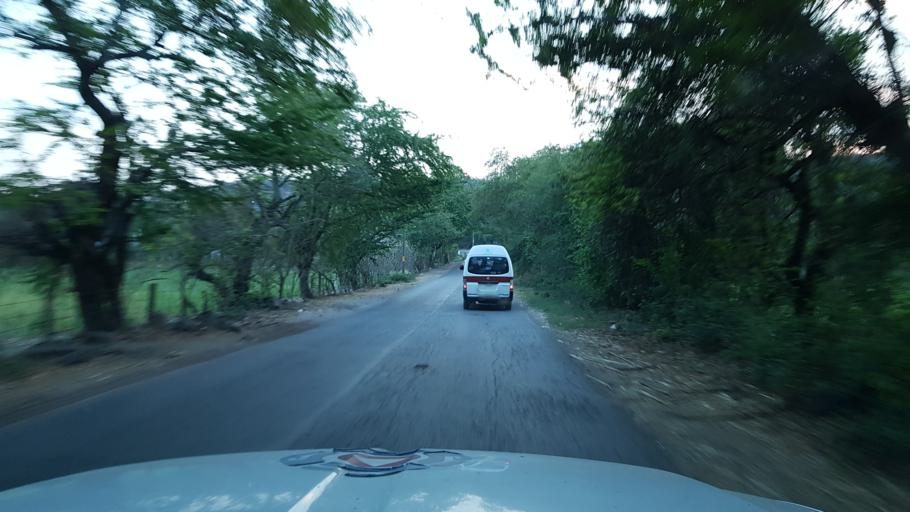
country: MX
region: Morelos
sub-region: Tlaltizapan de Zapata
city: Colonia Palo Prieto (Chipitongo)
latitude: 18.6984
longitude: -99.1122
